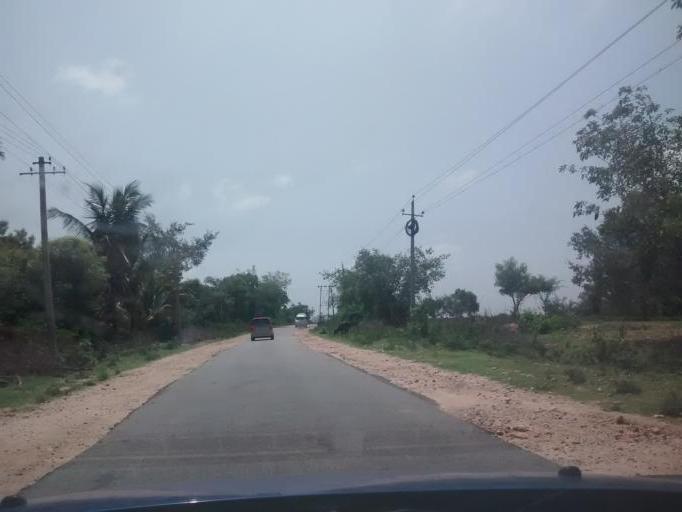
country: IN
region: Karnataka
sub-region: Mandya
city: Krishnarajpet
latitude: 12.5771
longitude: 76.3205
